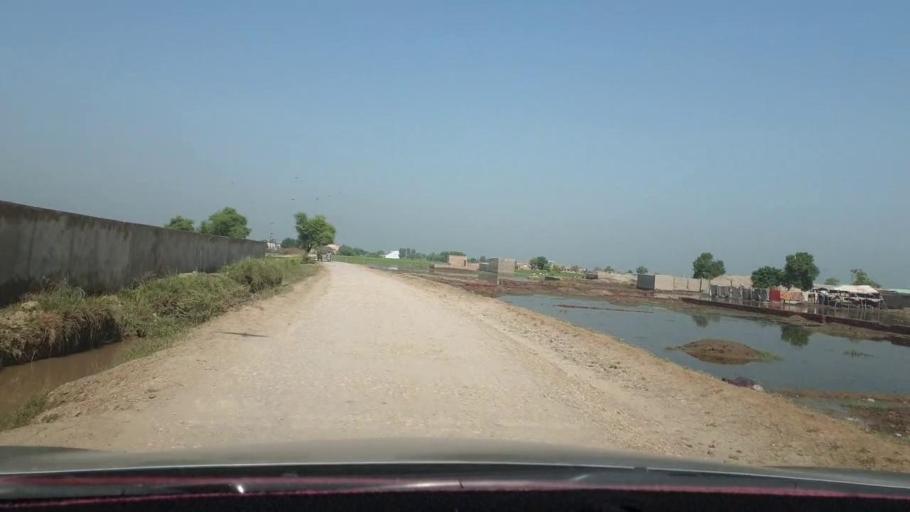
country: PK
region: Sindh
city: Kambar
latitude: 27.5982
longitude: 67.9846
